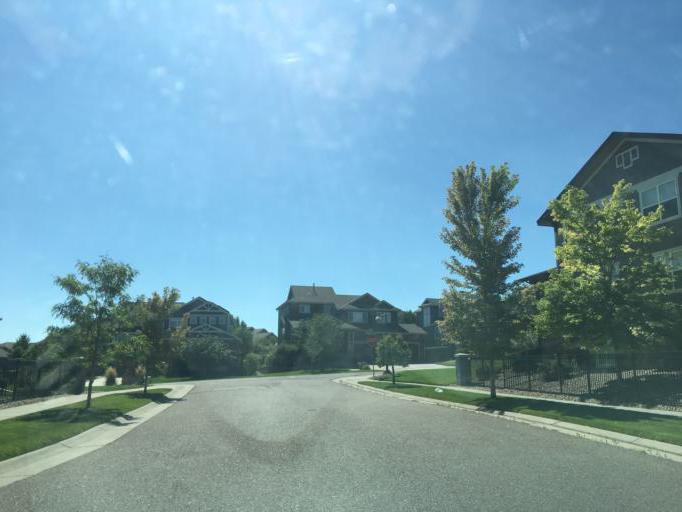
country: US
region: Colorado
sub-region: Douglas County
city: Parker
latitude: 39.6049
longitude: -104.6881
